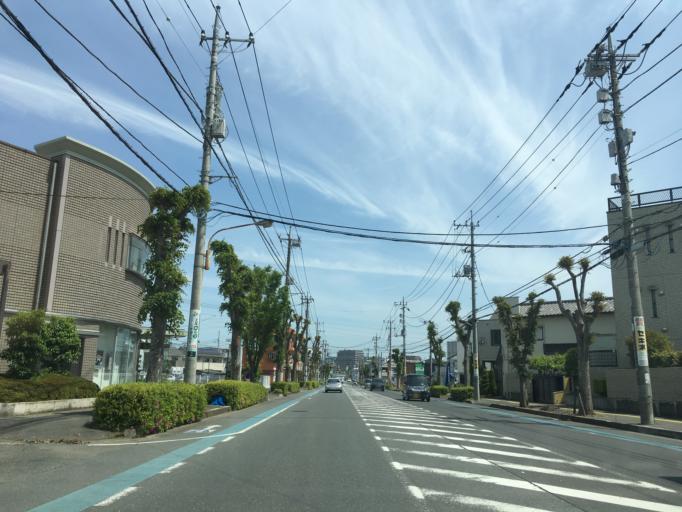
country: JP
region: Saitama
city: Ageoshimo
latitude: 35.9651
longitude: 139.5781
